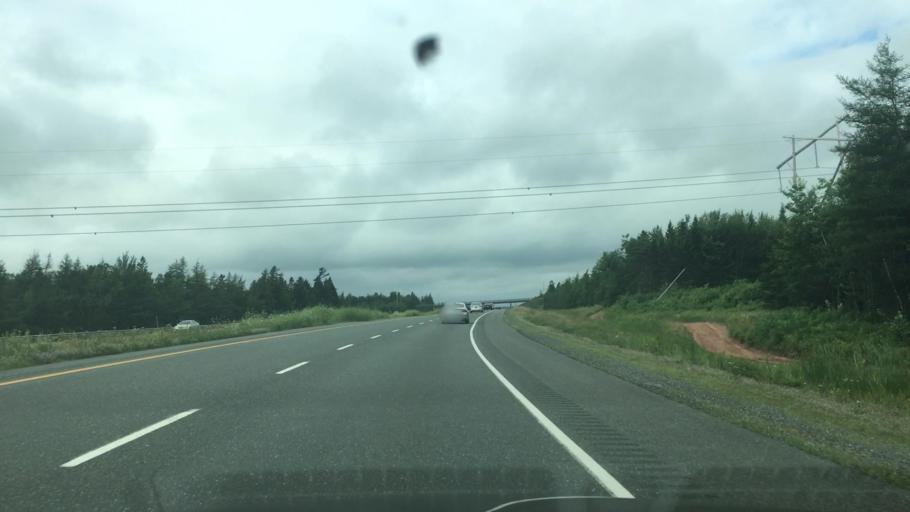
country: CA
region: Nova Scotia
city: Truro
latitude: 45.3817
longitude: -63.3601
